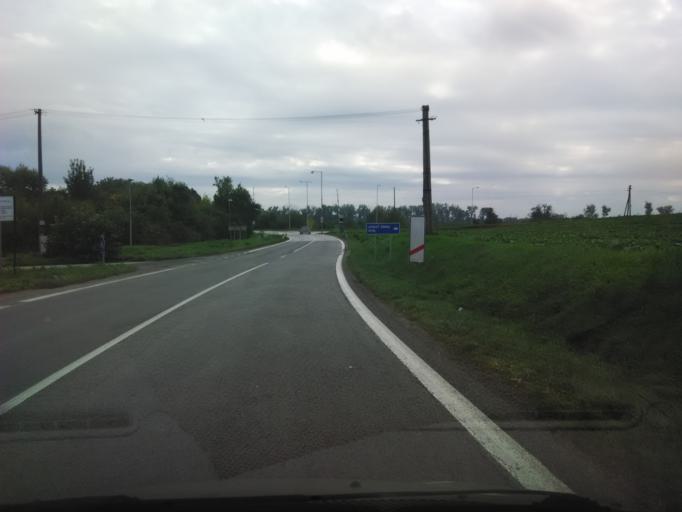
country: SK
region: Nitriansky
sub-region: Okres Nitra
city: Vrable
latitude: 48.2522
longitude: 18.2944
